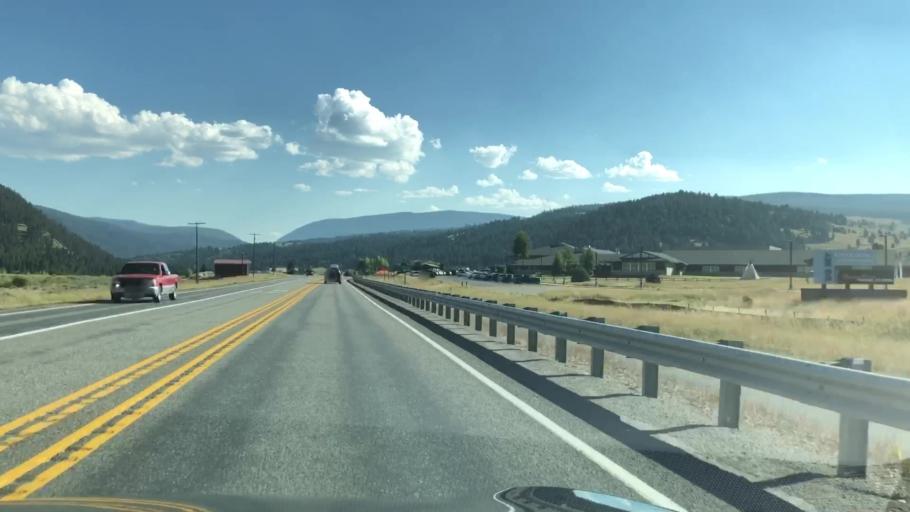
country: US
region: Montana
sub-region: Gallatin County
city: Big Sky
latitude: 45.2313
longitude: -111.2509
